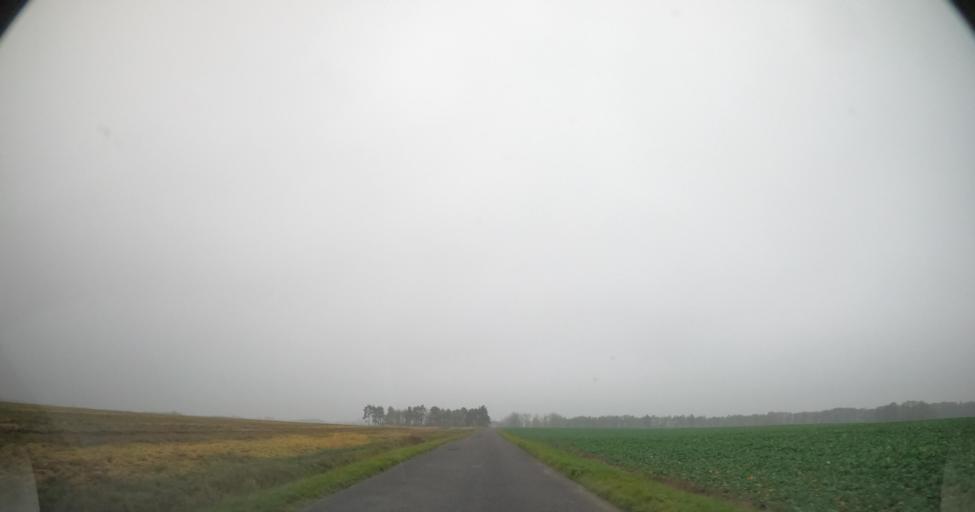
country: PL
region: West Pomeranian Voivodeship
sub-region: Powiat drawski
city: Drawsko Pomorskie
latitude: 53.6069
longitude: 15.7404
